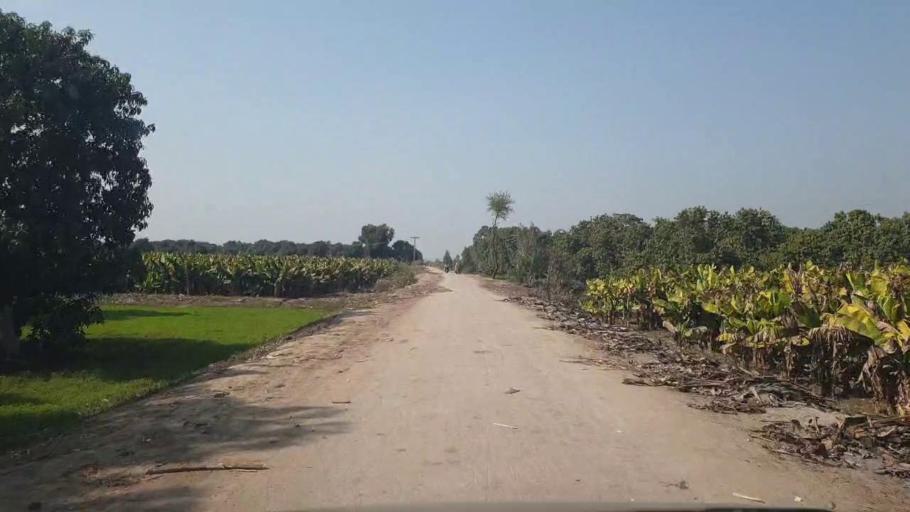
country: PK
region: Sindh
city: Tando Adam
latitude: 25.7694
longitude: 68.6027
